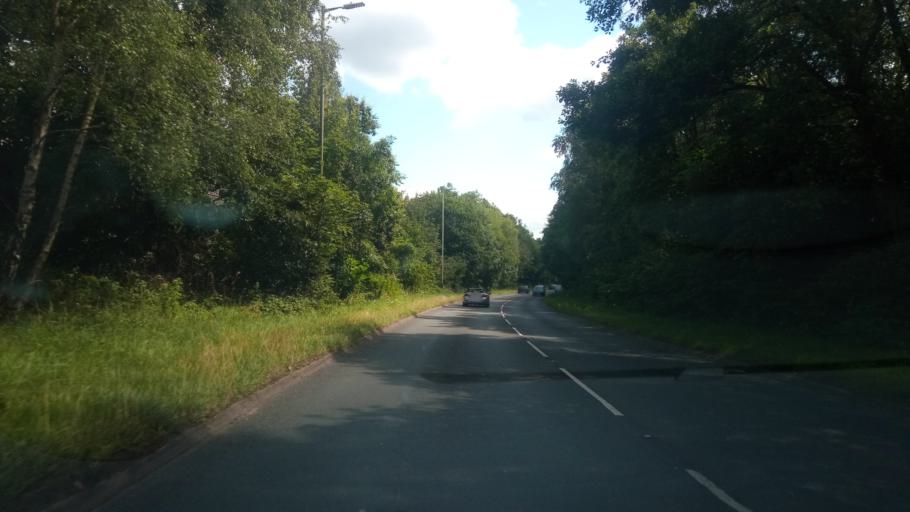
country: GB
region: Wales
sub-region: Caerphilly County Borough
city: Llanbradach
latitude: 51.5927
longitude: -3.2210
